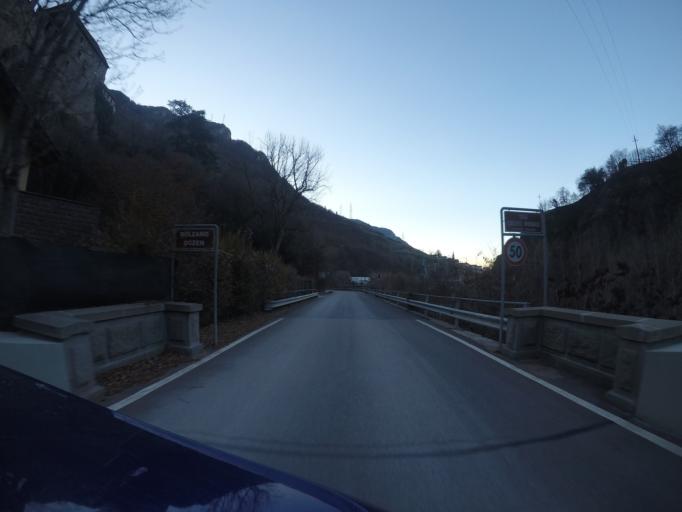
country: IT
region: Trentino-Alto Adige
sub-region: Bolzano
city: Bolzano
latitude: 46.5178
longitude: 11.3580
